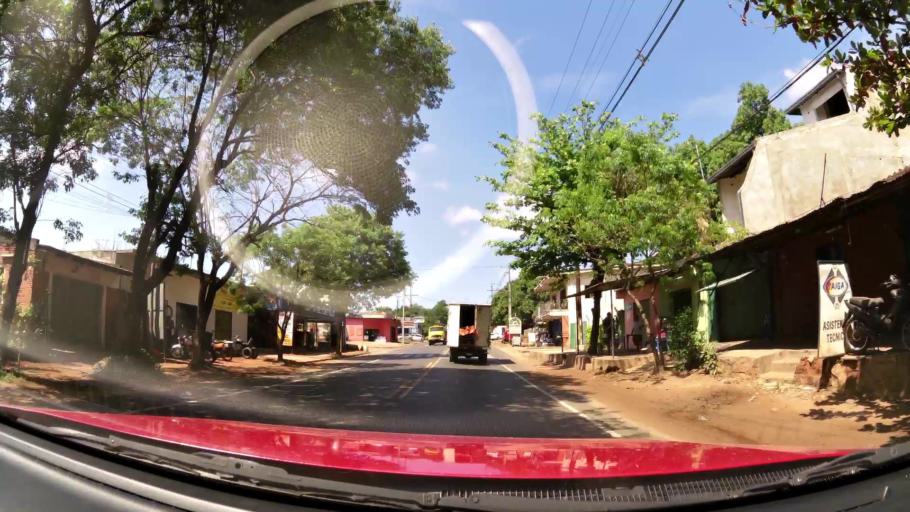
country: PY
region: Central
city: San Lorenzo
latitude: -25.3174
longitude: -57.5076
